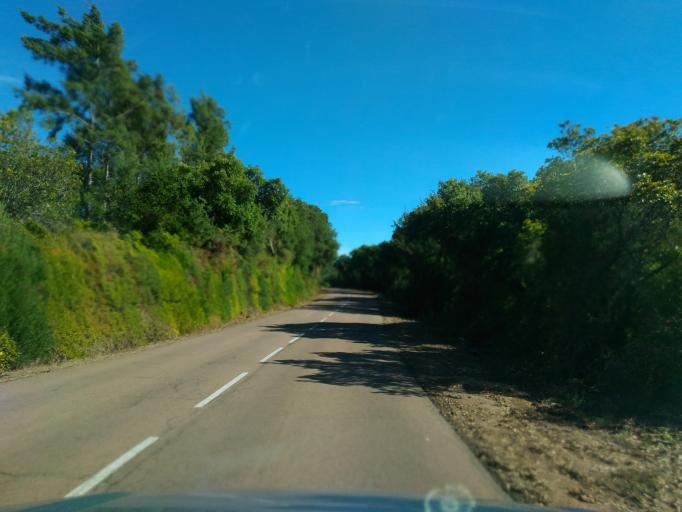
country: FR
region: Corsica
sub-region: Departement de la Corse-du-Sud
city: Porto-Vecchio
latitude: 41.6947
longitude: 9.3663
